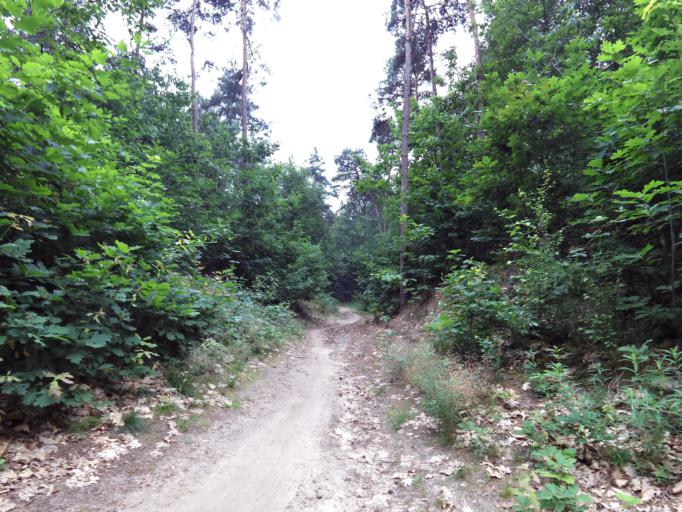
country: NL
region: North Brabant
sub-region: Gemeente Cuijk
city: Cuijk
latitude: 51.7569
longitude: 5.8855
